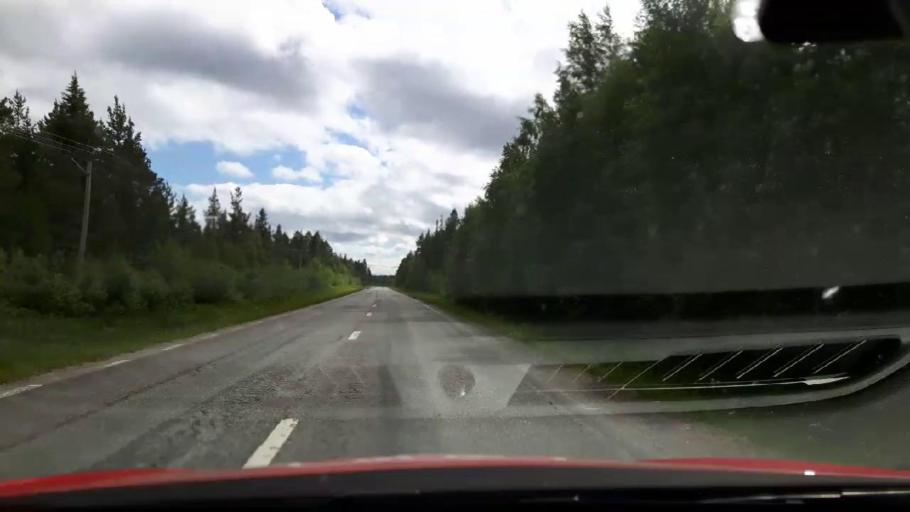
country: SE
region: Jaemtland
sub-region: Ragunda Kommun
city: Hammarstrand
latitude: 63.0073
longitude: 16.1170
